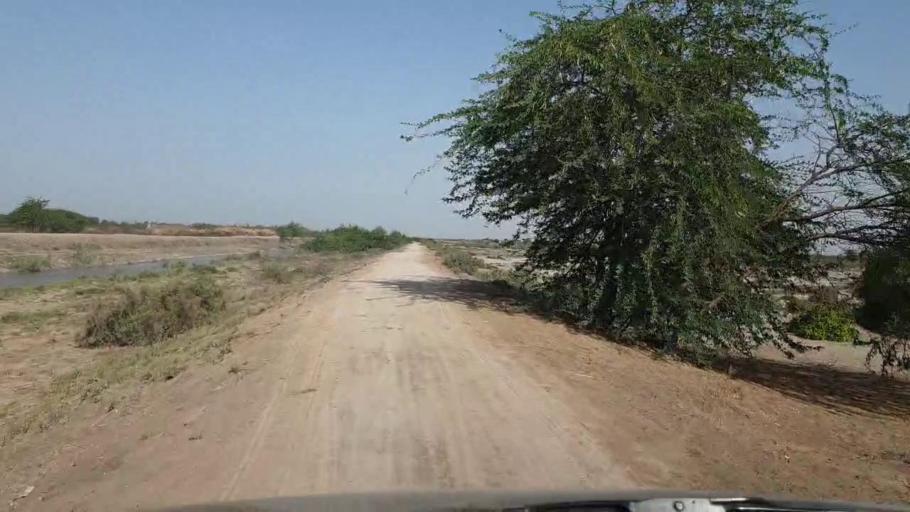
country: PK
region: Sindh
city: Tando Bago
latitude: 24.6415
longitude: 69.0723
